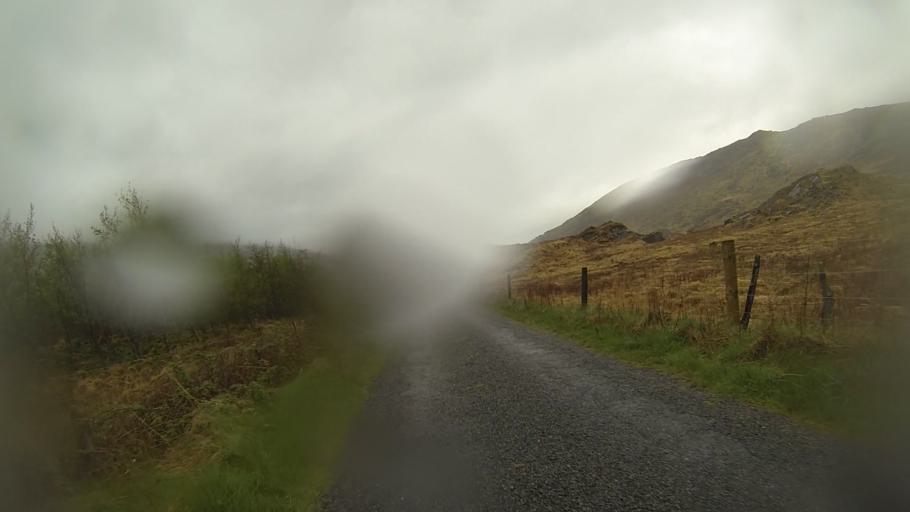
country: IE
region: Munster
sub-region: Ciarrai
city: Kenmare
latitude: 51.9490
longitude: -9.6852
